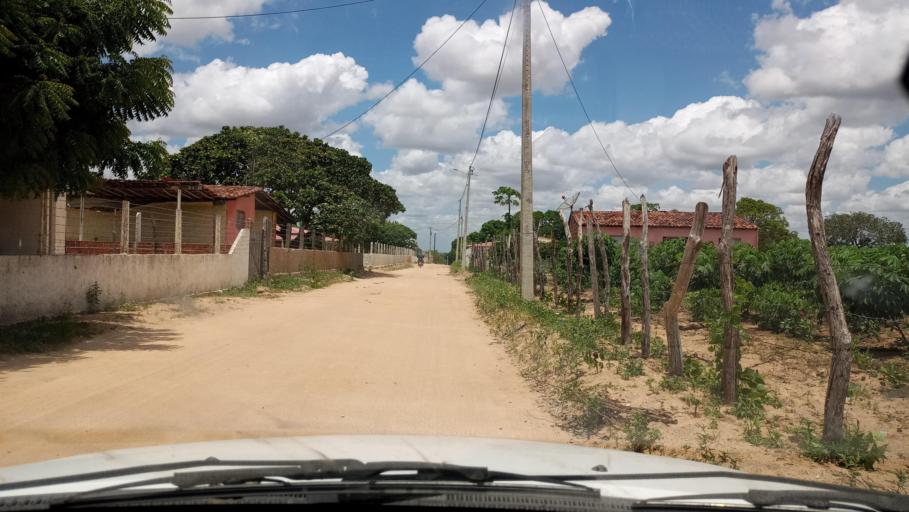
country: BR
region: Rio Grande do Norte
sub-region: Sao Jose Do Campestre
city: Sao Jose do Campestre
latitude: -6.4307
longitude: -35.6297
